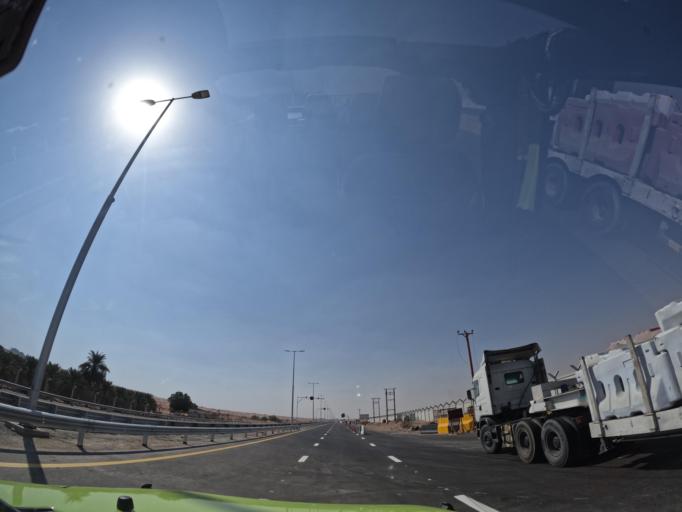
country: AE
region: Ash Shariqah
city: Adh Dhayd
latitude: 24.7724
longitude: 55.8113
